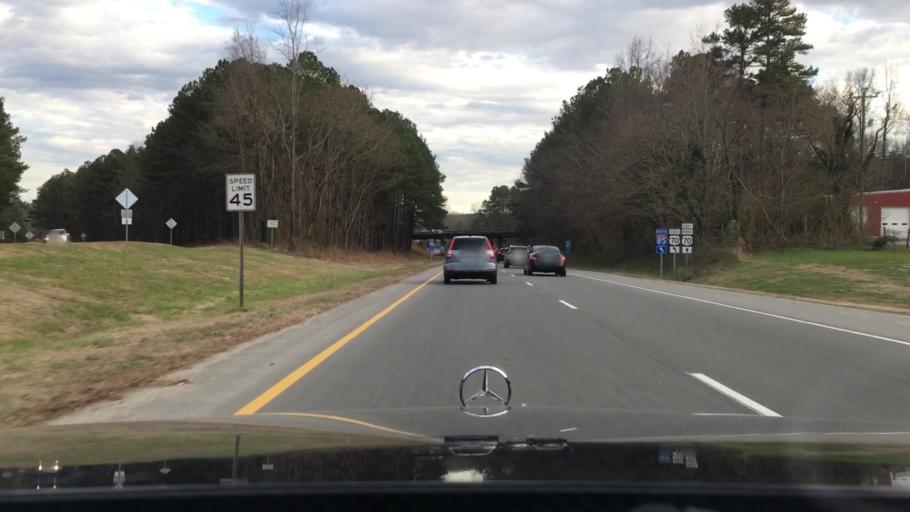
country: US
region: North Carolina
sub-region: Orange County
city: Hillsborough
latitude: 36.0405
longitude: -79.0138
